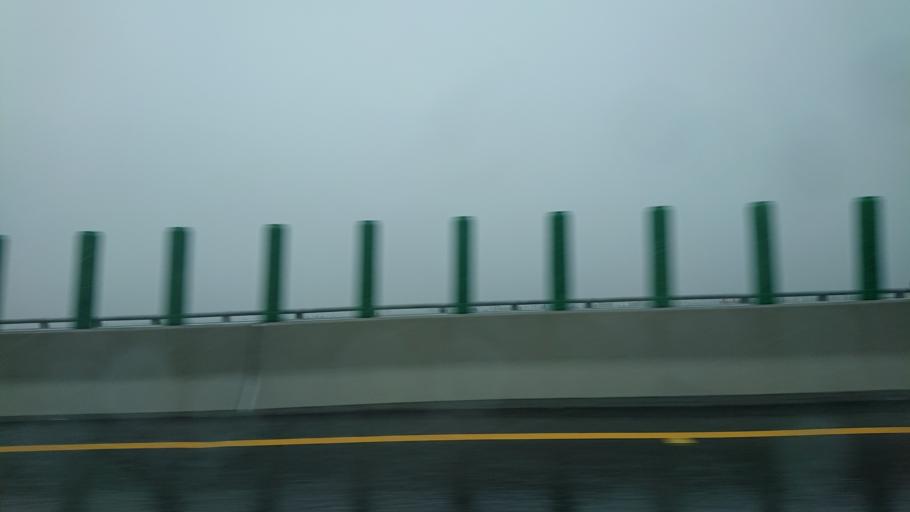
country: TW
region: Taiwan
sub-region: Changhua
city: Chang-hua
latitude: 23.9102
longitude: 120.3070
